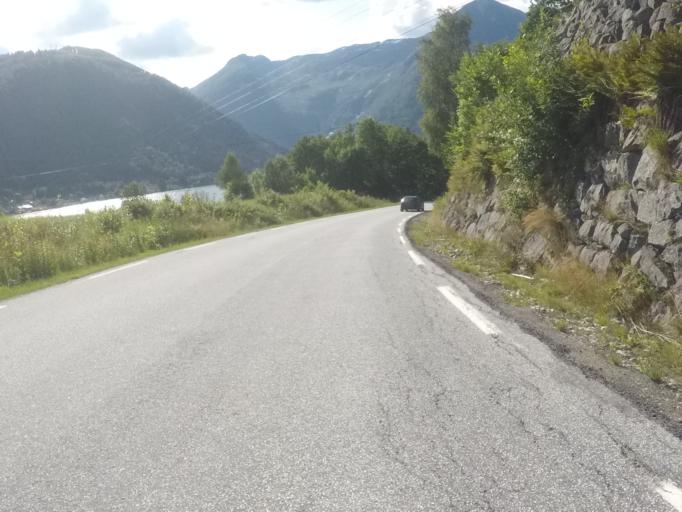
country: NO
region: Sogn og Fjordane
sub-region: Balestrand
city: Balestrand
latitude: 61.2155
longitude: 6.5406
